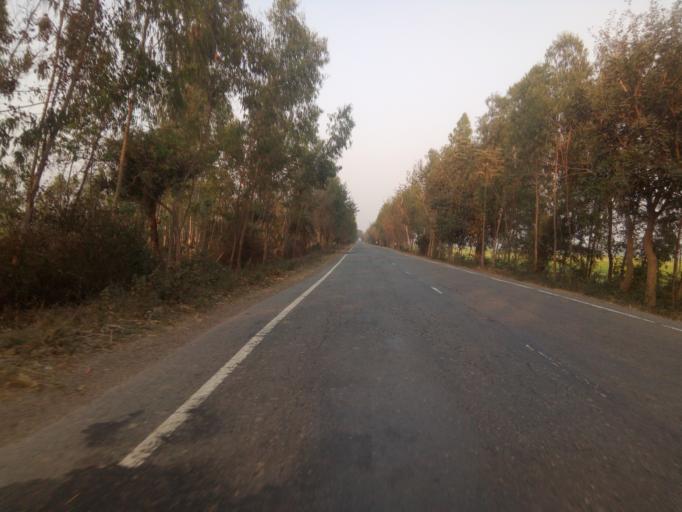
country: BD
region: Rajshahi
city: Bogra
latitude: 24.5738
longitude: 89.2177
